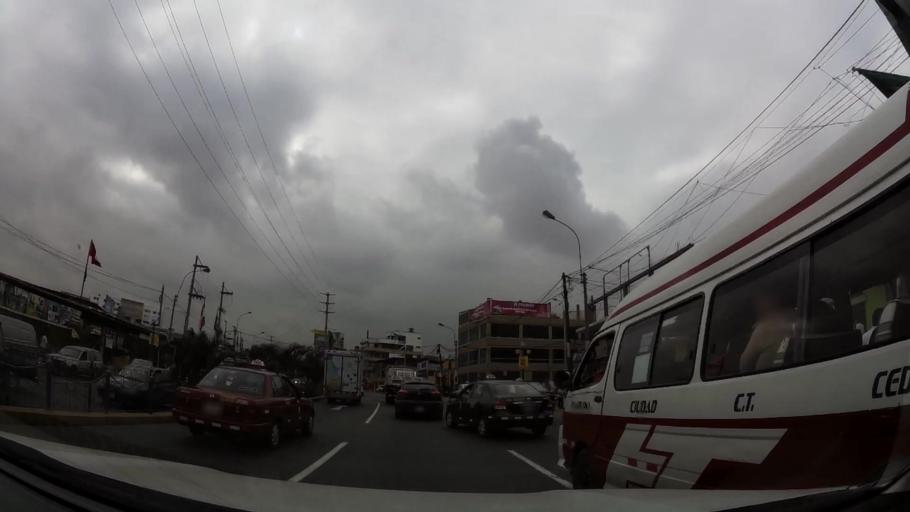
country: PE
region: Lima
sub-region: Lima
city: Surco
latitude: -12.1835
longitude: -77.0006
